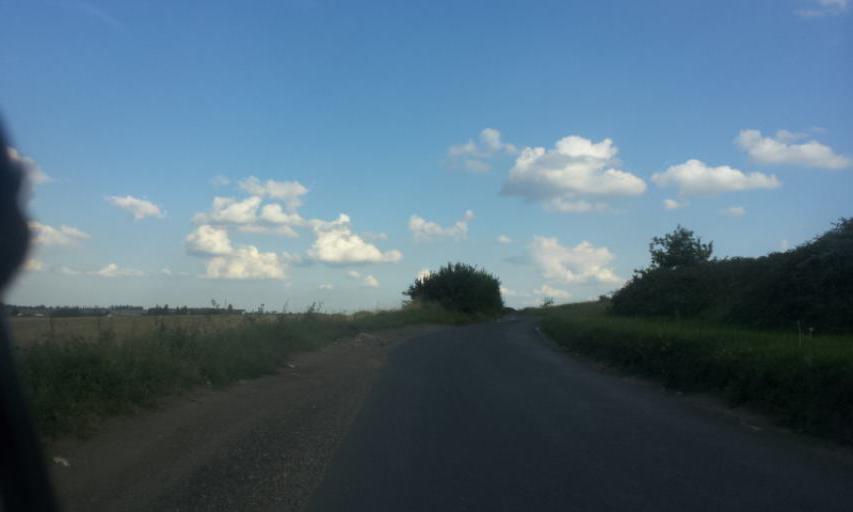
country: GB
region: England
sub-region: Kent
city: Eynsford
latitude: 51.4044
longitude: 0.2172
